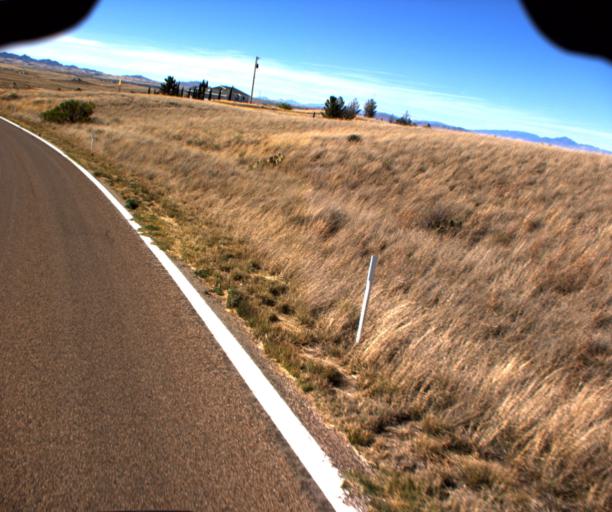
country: US
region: Arizona
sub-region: Cochise County
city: Huachuca City
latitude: 31.6678
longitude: -110.6059
